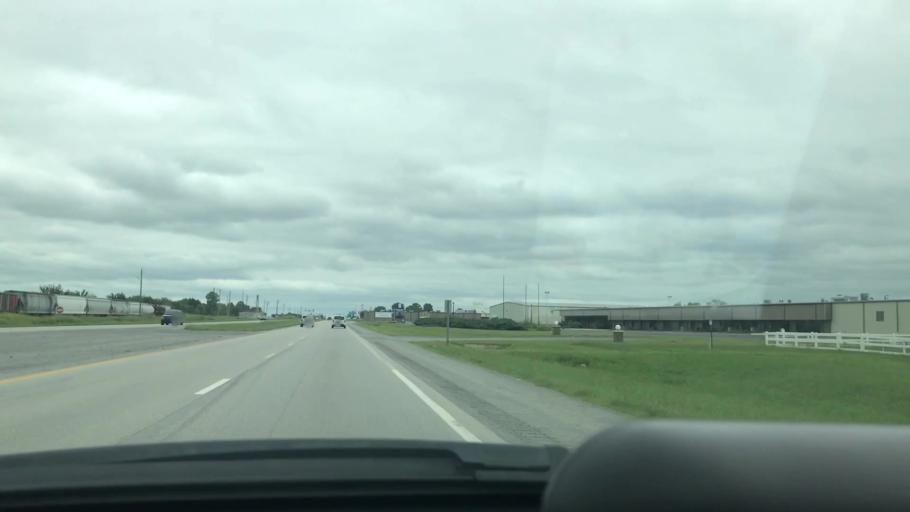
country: US
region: Oklahoma
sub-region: Mayes County
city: Chouteau
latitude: 36.2387
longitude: -95.3378
